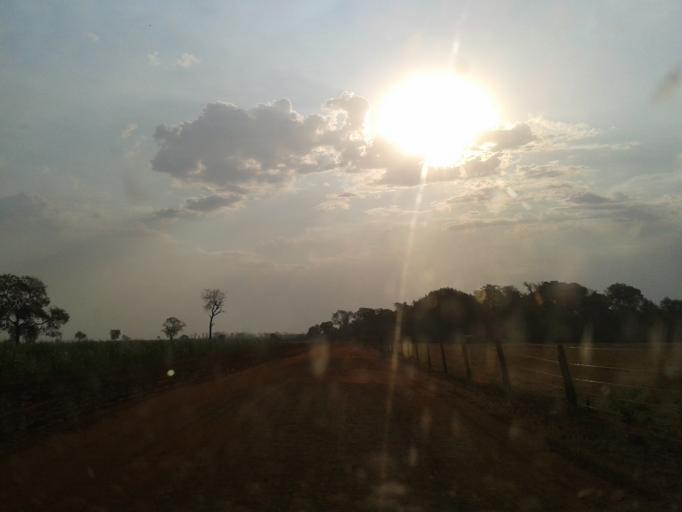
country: BR
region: Minas Gerais
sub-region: Capinopolis
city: Capinopolis
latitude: -18.7560
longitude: -49.7082
